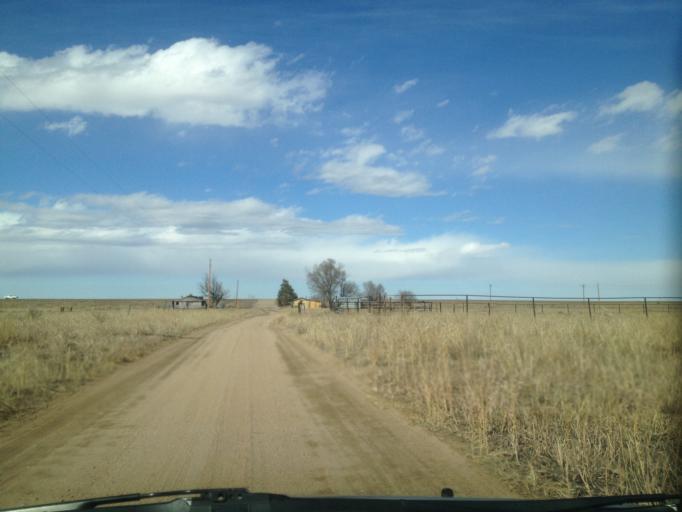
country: US
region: Colorado
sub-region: Weld County
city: Keenesburg
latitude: 40.2888
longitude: -104.2591
